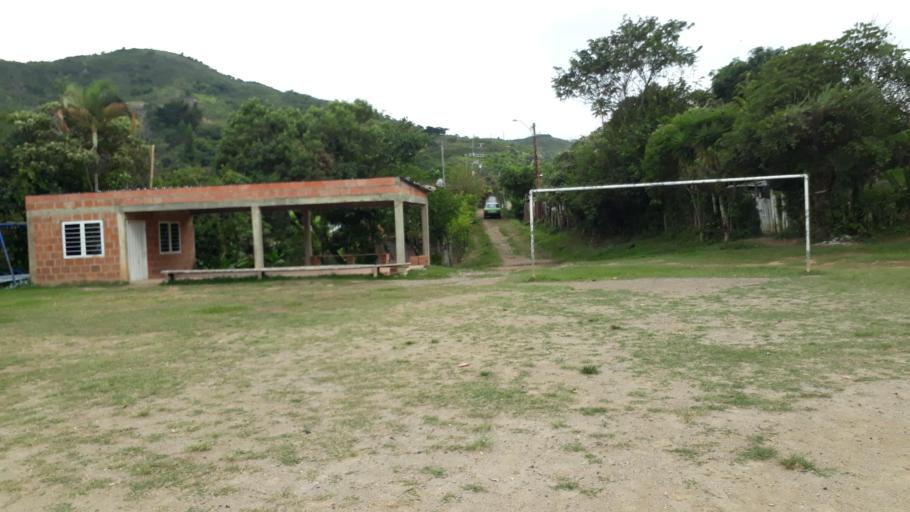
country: CO
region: Valle del Cauca
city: Jamundi
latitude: 3.2063
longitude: -76.6306
